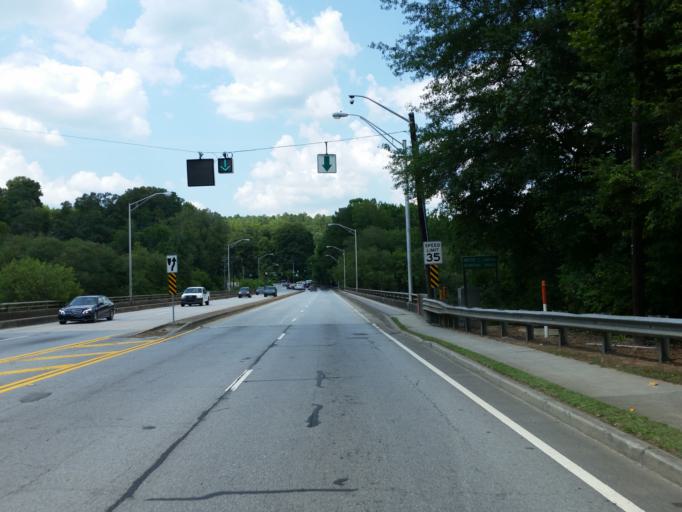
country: US
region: Georgia
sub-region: Fulton County
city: Roswell
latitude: 34.0032
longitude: -84.3504
